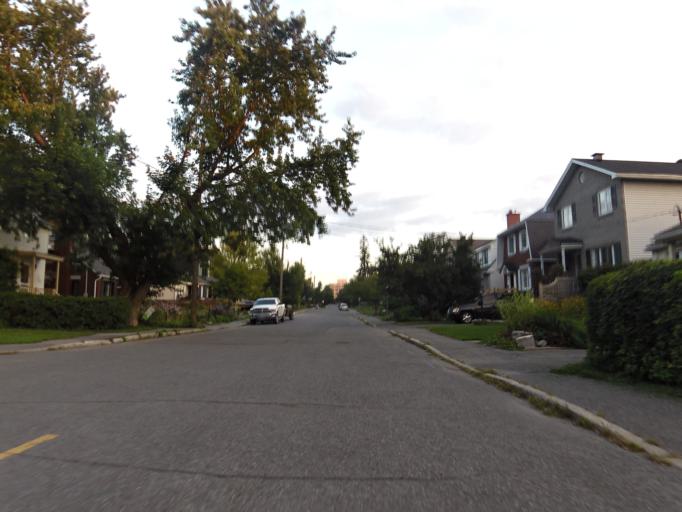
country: CA
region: Ontario
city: Ottawa
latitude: 45.4019
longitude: -75.7382
